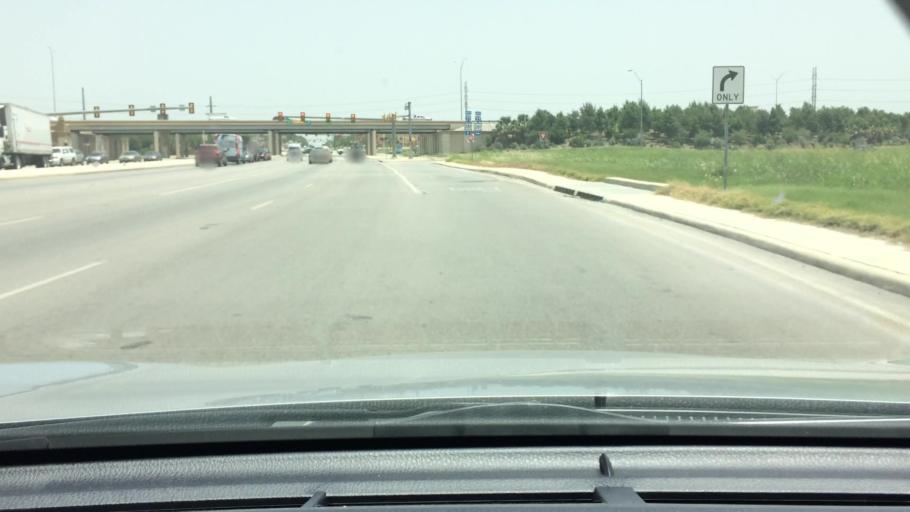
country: US
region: Texas
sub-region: Bexar County
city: China Grove
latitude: 29.3520
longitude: -98.4300
